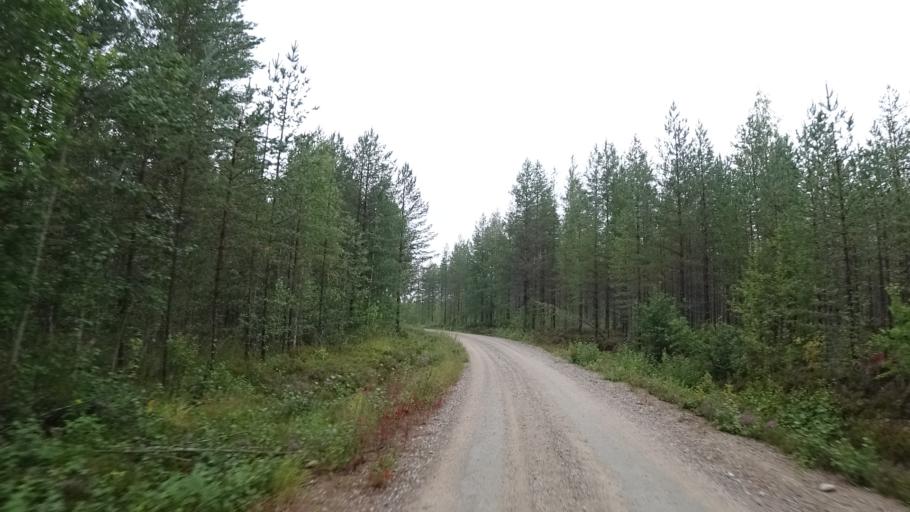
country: FI
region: North Karelia
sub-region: Pielisen Karjala
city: Lieksa
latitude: 63.5120
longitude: 30.1378
